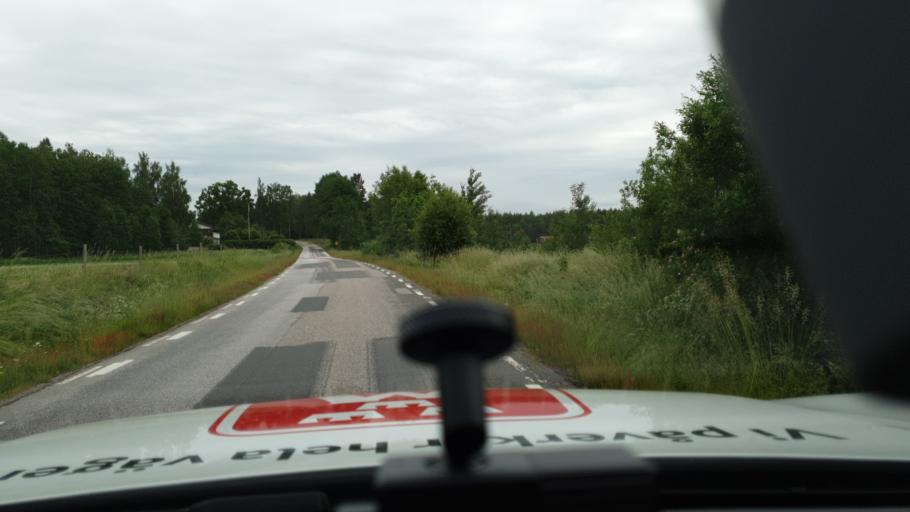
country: SE
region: Vaestra Goetaland
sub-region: Skovde Kommun
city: Stopen
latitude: 58.5726
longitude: 13.8489
